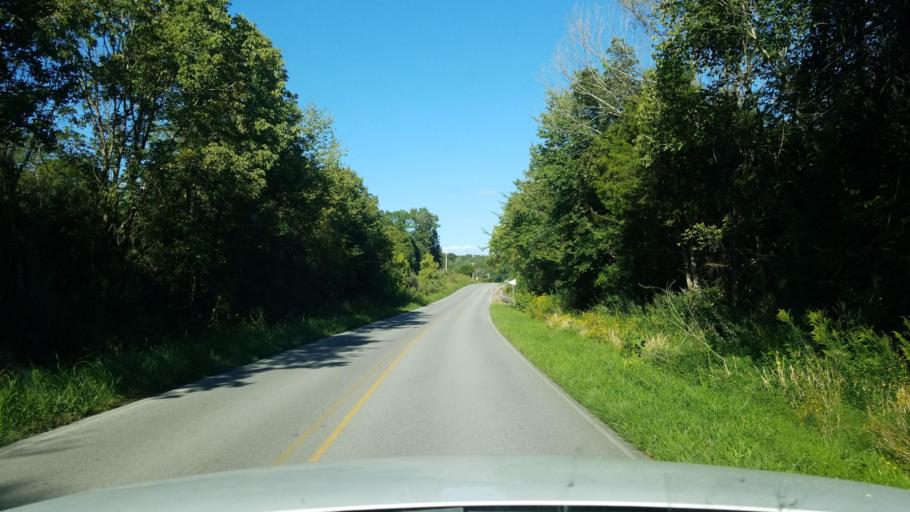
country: US
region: Illinois
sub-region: Hardin County
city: Elizabethtown
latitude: 37.5799
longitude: -88.3728
